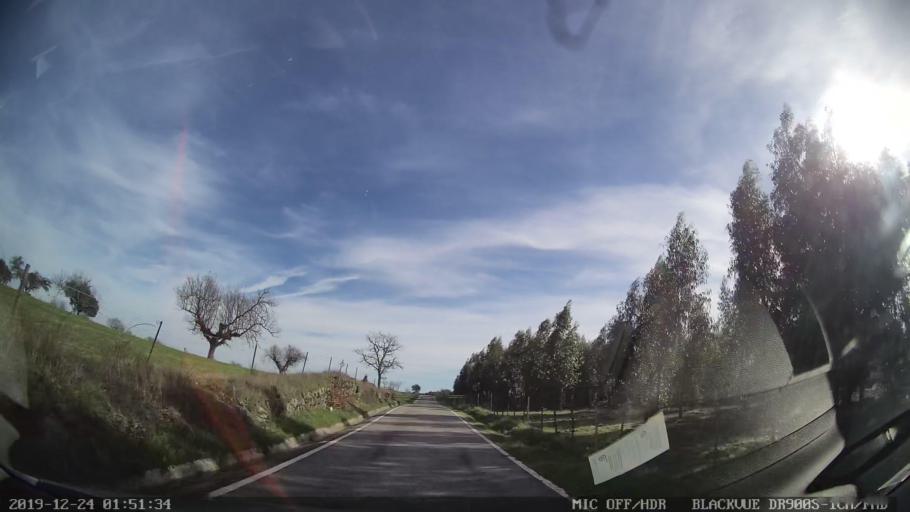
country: PT
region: Portalegre
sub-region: Nisa
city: Nisa
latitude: 39.4963
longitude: -7.7559
